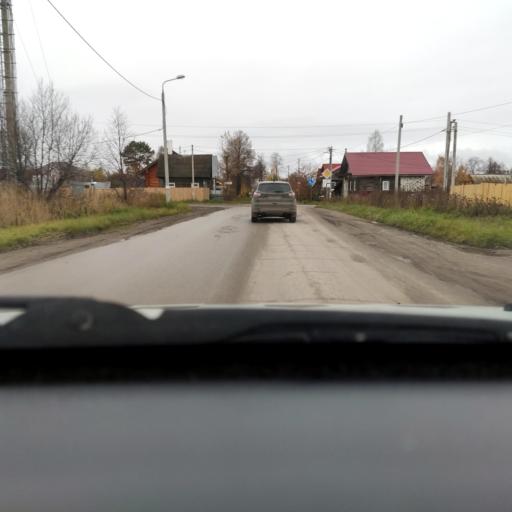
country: RU
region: Perm
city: Perm
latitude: 58.0211
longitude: 56.3353
